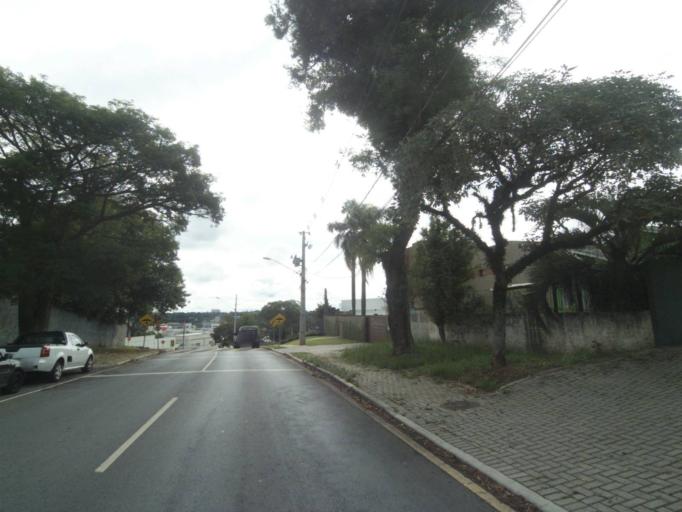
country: BR
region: Parana
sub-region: Curitiba
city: Curitiba
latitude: -25.4418
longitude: -49.3022
